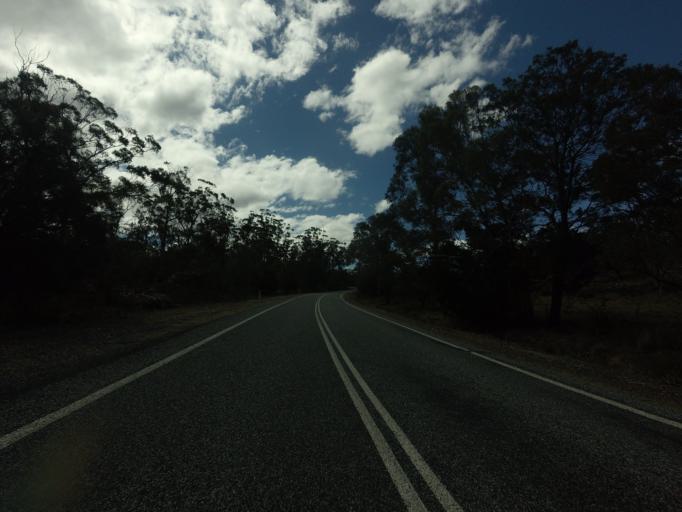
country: AU
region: Tasmania
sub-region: Break O'Day
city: St Helens
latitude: -42.0194
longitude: 148.0066
